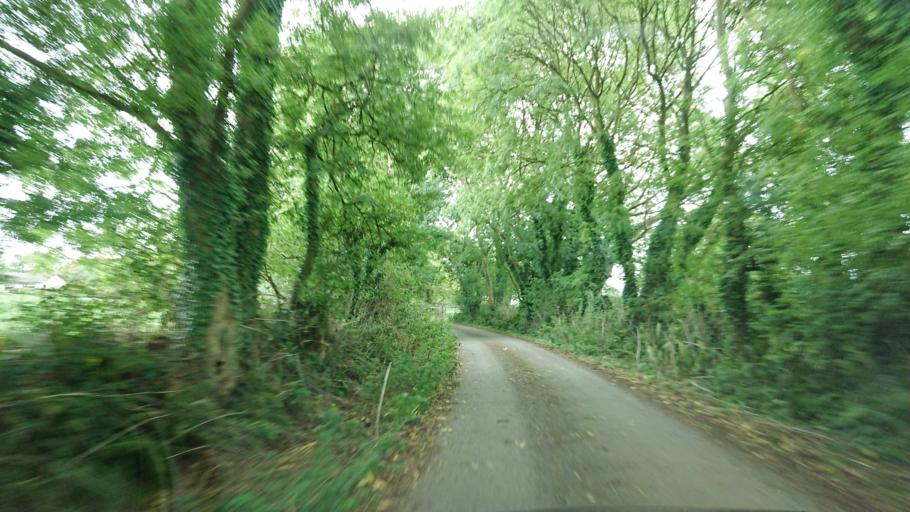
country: IE
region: Munster
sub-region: Waterford
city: Dunmore East
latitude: 52.2021
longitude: -7.0450
